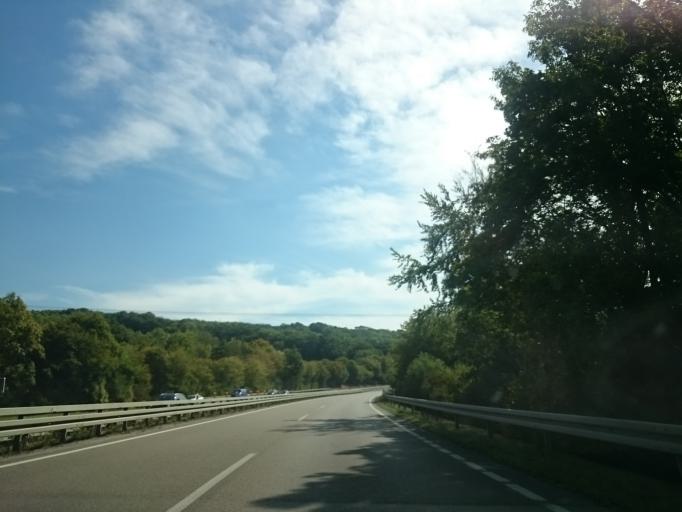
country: DE
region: Bavaria
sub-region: Swabia
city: Donauwoerth
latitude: 48.7369
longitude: 10.7791
